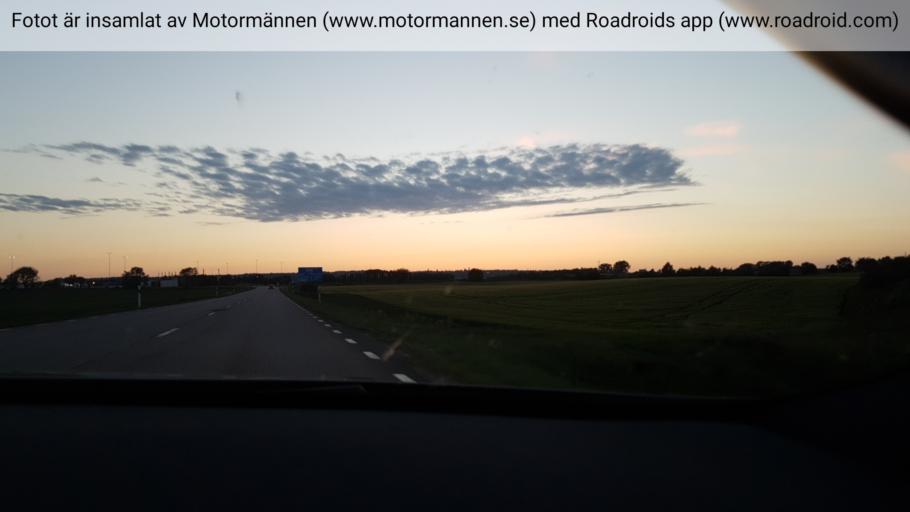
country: SE
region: Vaestra Goetaland
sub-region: Falkopings Kommun
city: Falkoeping
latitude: 58.1580
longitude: 13.5820
